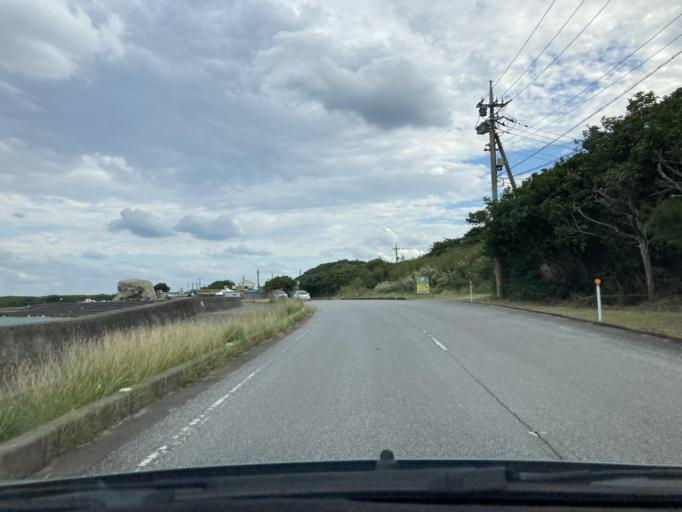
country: JP
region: Okinawa
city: Katsuren-haebaru
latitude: 26.3247
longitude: 127.9635
